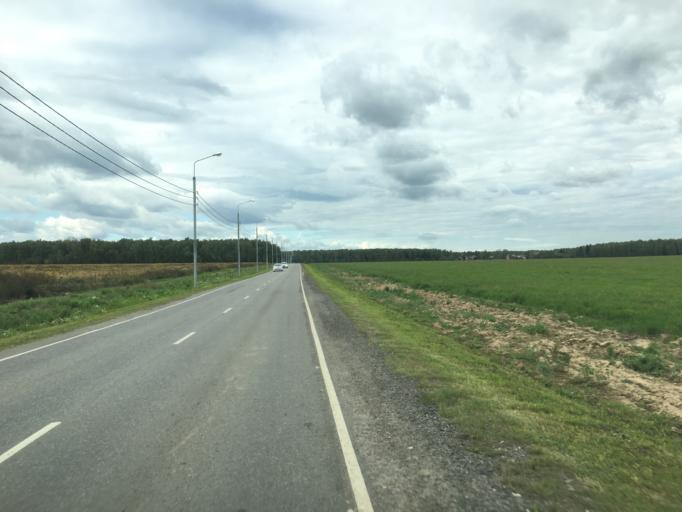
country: RU
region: Moskovskaya
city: Vatutinki
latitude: 55.4927
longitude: 37.3988
